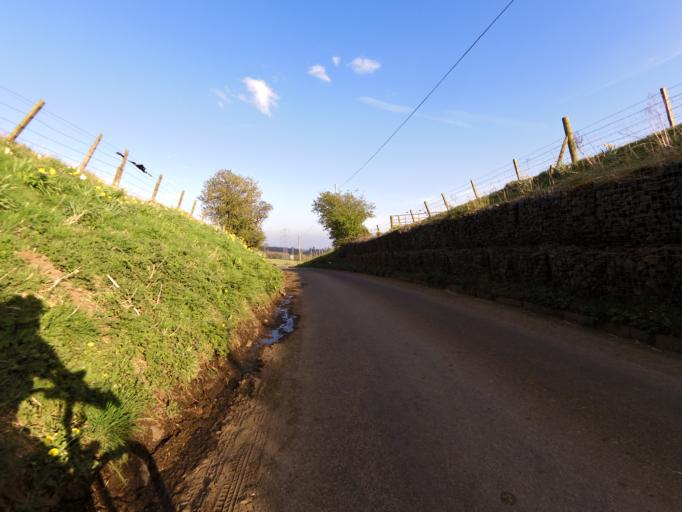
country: GB
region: Scotland
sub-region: Fife
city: Leslie
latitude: 56.2117
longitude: -3.2103
